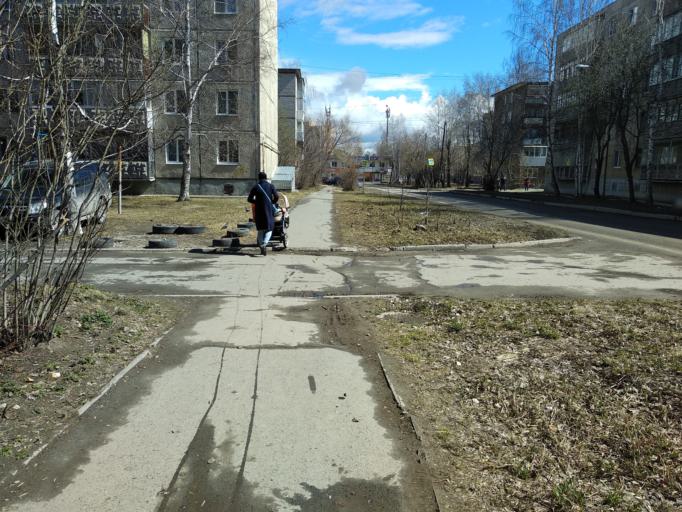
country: RU
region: Sverdlovsk
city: Beryozovsky
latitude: 56.8996
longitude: 60.7464
